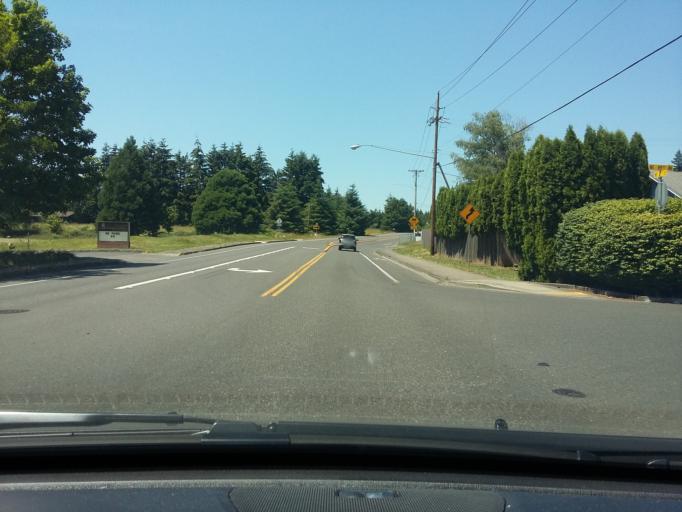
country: US
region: Washington
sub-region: Clark County
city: Five Corners
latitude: 45.6778
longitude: -122.5818
